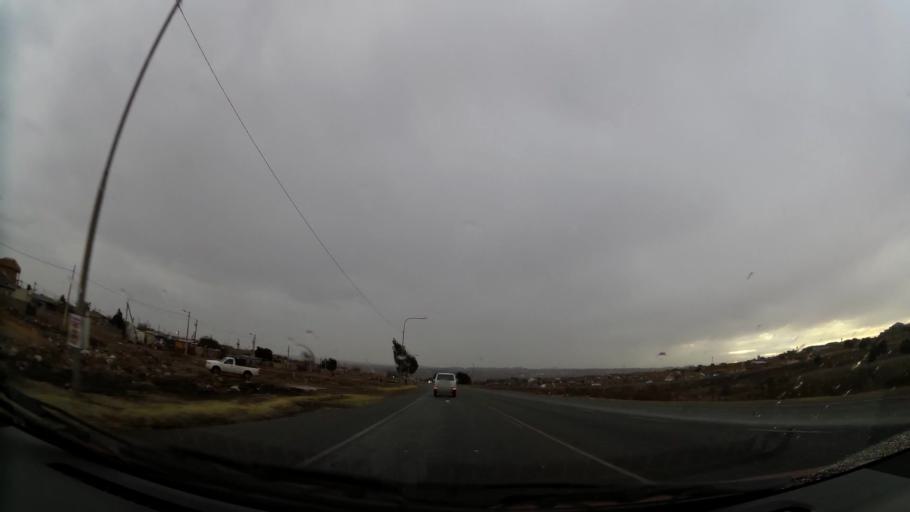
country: ZA
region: Gauteng
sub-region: West Rand District Municipality
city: Randfontein
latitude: -26.1718
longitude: 27.7867
